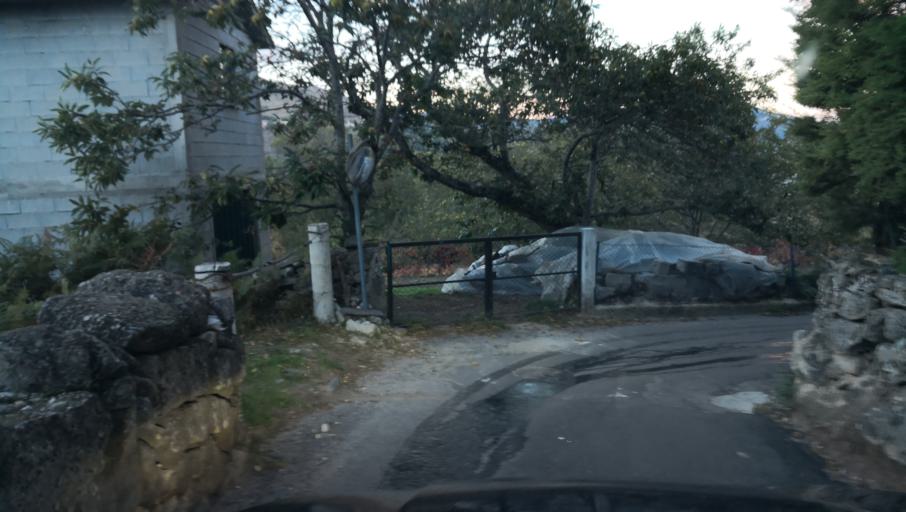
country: PT
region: Vila Real
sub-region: Santa Marta de Penaguiao
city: Santa Marta de Penaguiao
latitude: 41.2749
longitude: -7.8123
